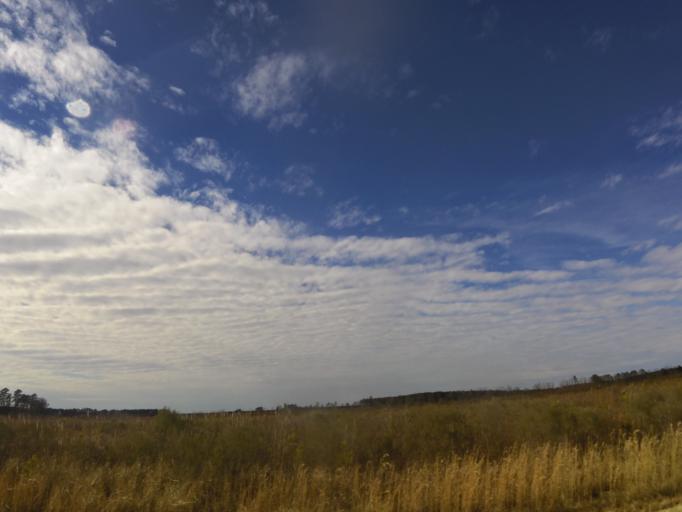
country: US
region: Virginia
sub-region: City of Franklin
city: Franklin
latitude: 36.6978
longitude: -76.8932
